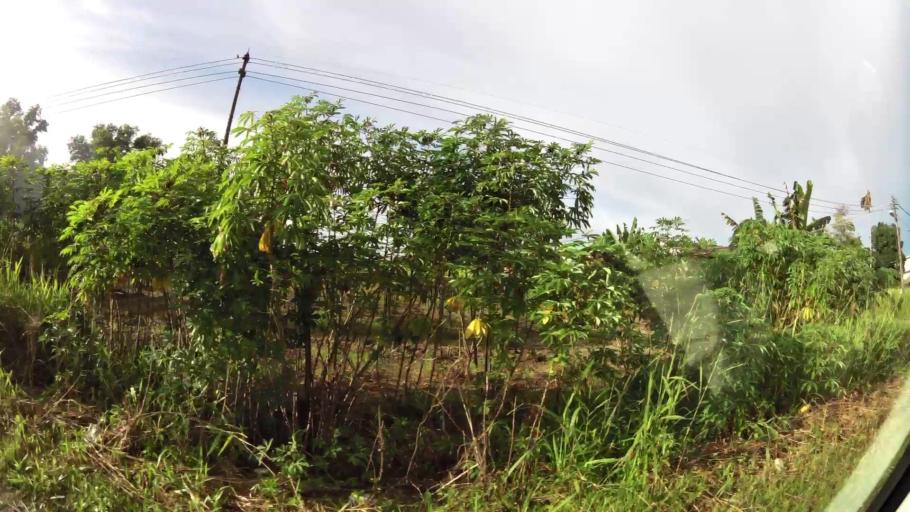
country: BN
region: Brunei and Muara
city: Bandar Seri Begawan
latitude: 4.9641
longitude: 115.0211
